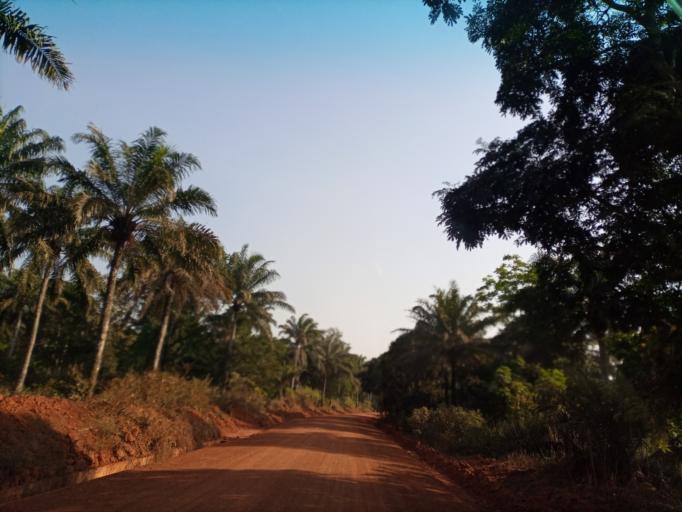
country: NG
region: Enugu
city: Opi
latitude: 6.7761
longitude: 7.3900
